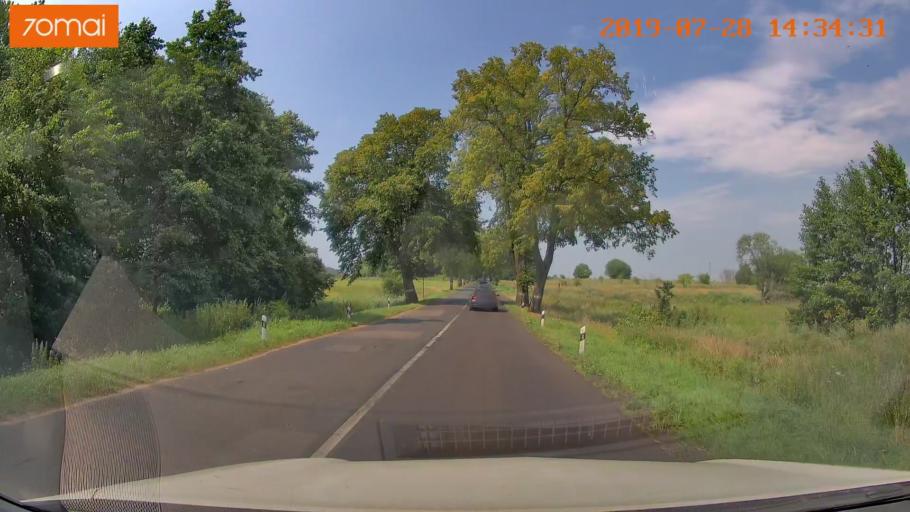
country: RU
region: Kaliningrad
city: Primorsk
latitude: 54.8257
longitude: 20.0176
